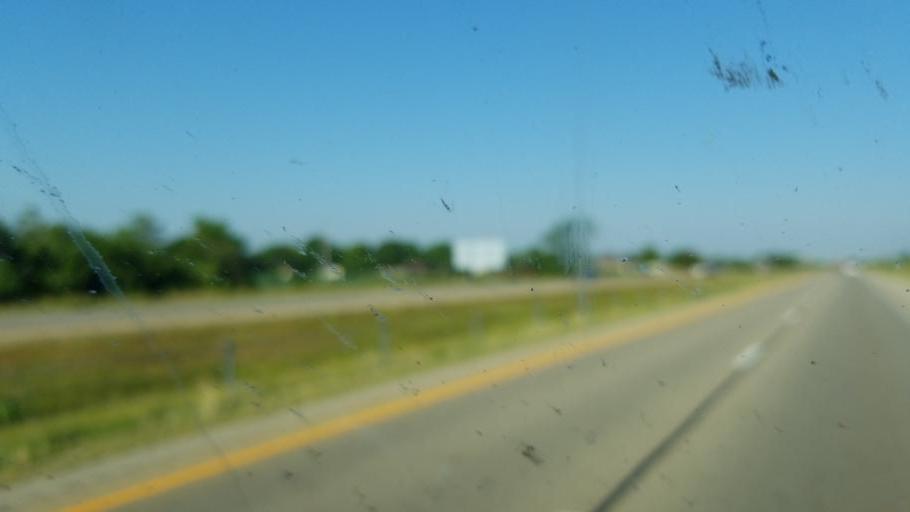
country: US
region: Illinois
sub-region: LaSalle County
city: Ottawa
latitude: 41.3686
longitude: -88.8671
